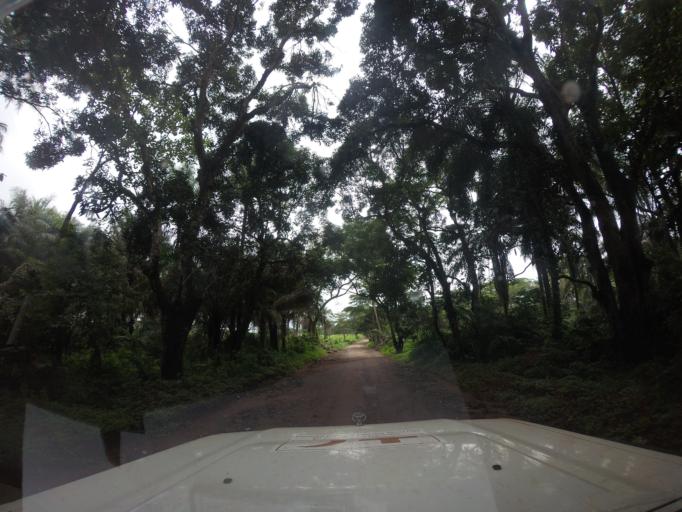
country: SL
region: Northern Province
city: Kukuna
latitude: 9.2750
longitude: -12.6754
